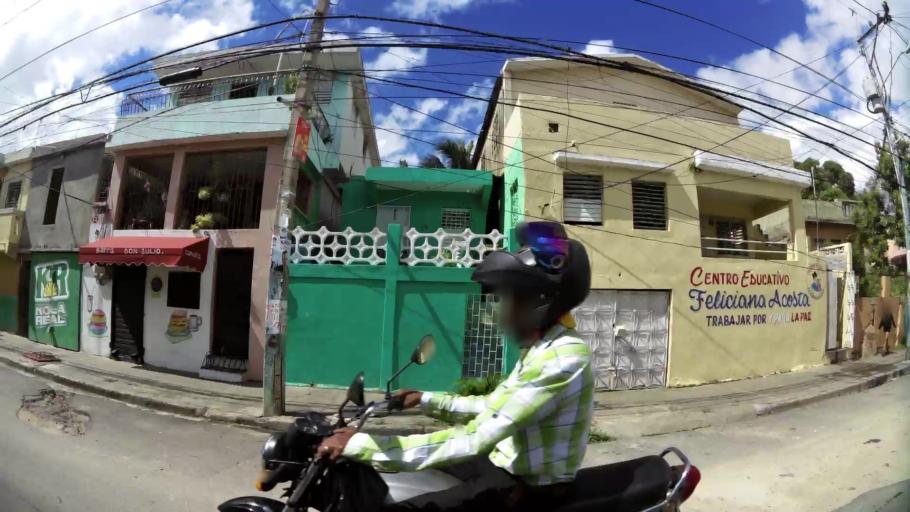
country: DO
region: Nacional
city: San Carlos
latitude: 18.4908
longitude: -69.8861
